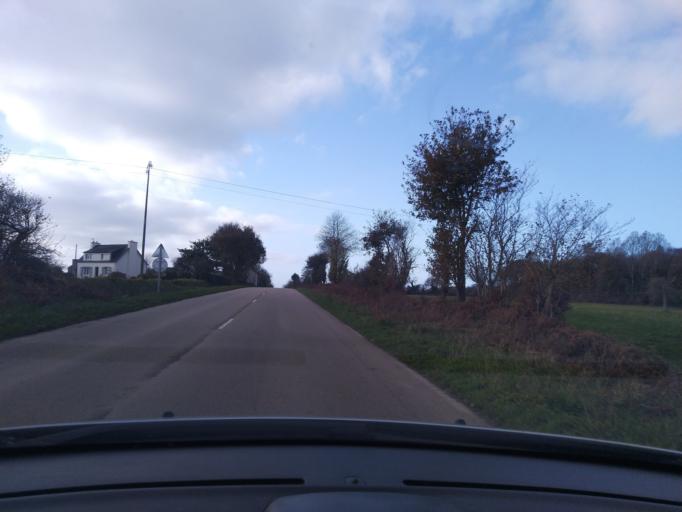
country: FR
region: Brittany
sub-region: Departement du Finistere
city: Plourin-les-Morlaix
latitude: 48.5763
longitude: -3.7711
